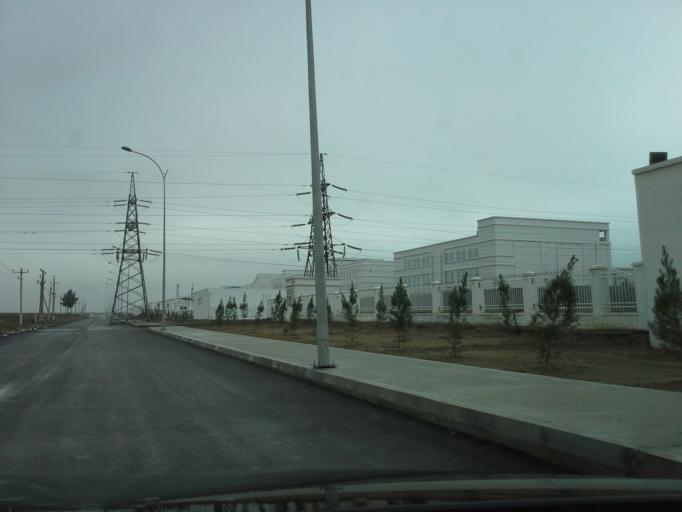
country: TM
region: Ahal
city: Ashgabat
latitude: 37.9587
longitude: 58.4243
